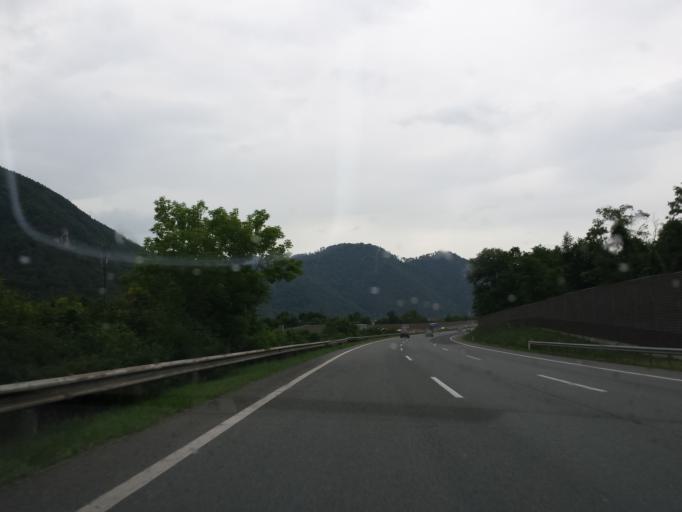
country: AT
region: Styria
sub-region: Politischer Bezirk Graz-Umgebung
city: Gratkorn
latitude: 47.1461
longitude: 15.3308
